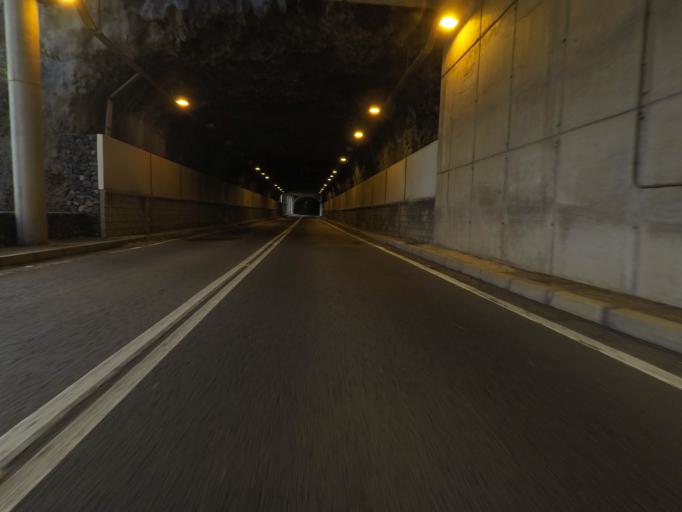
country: ES
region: Canary Islands
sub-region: Provincia de Santa Cruz de Tenerife
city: Hermigua
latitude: 28.1266
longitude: -17.1658
